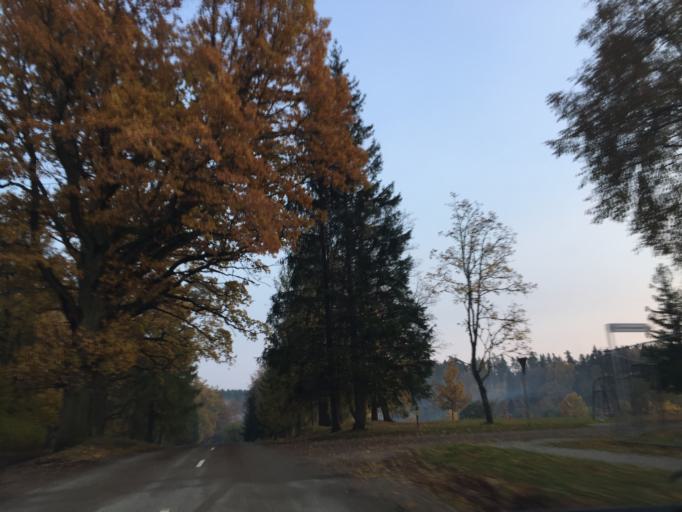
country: LV
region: Cesu Rajons
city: Cesis
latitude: 57.3111
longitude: 25.1608
